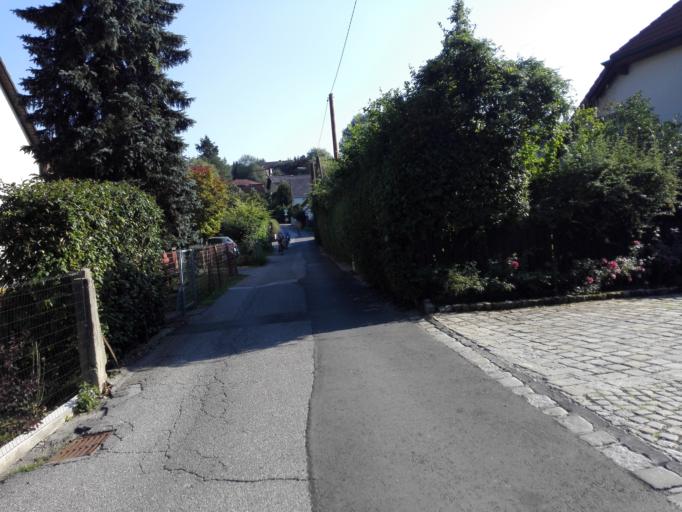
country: AT
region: Styria
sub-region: Graz Stadt
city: Mariatrost
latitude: 47.0771
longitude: 15.4876
